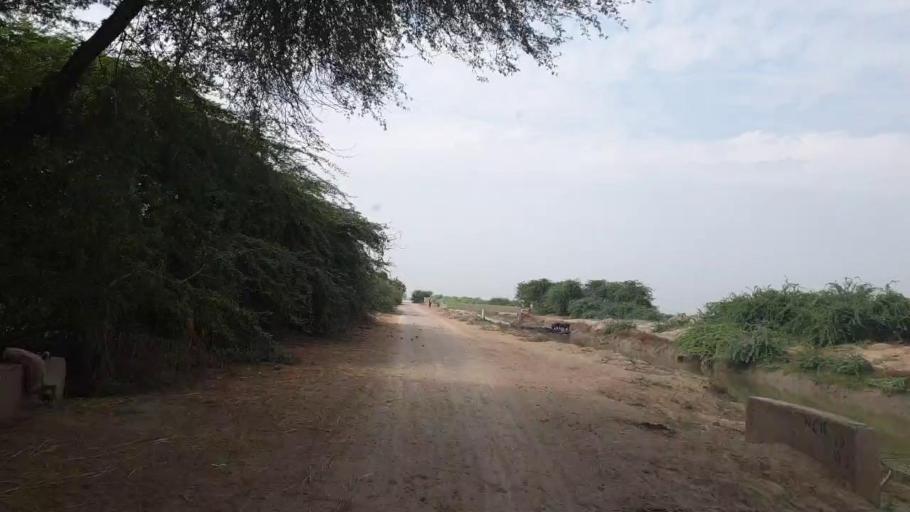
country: PK
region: Sindh
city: Kario
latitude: 24.6224
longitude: 68.5803
